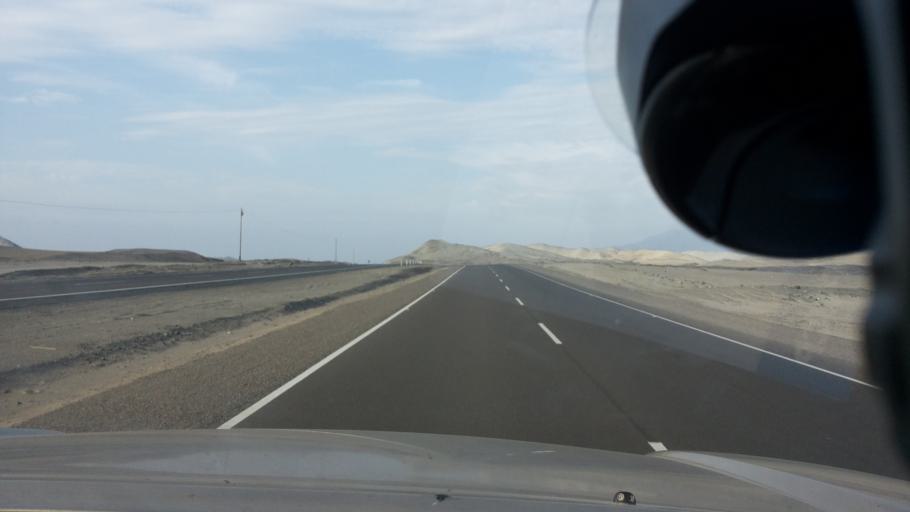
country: PE
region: Ancash
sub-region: Provincia de Casma
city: Casma
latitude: -9.6492
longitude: -78.2602
